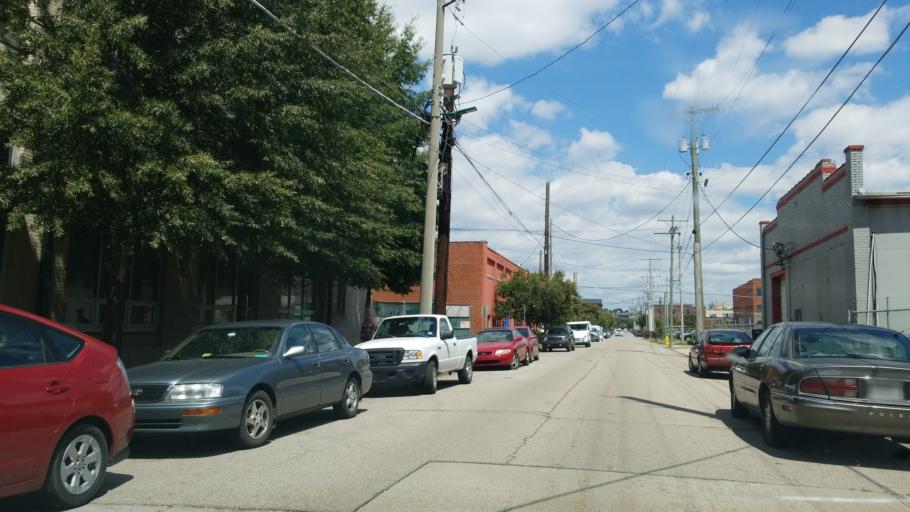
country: US
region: Tennessee
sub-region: Hamilton County
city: Chattanooga
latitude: 35.0356
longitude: -85.3111
